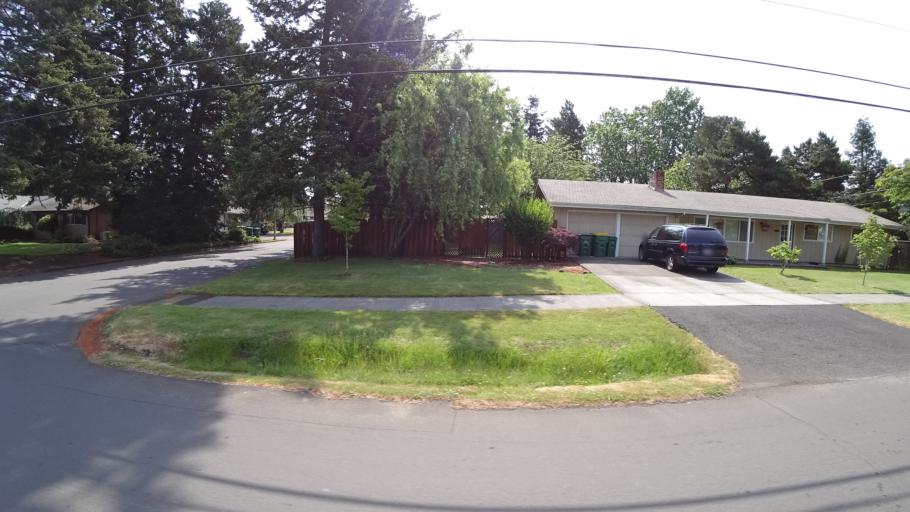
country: US
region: Oregon
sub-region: Washington County
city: Cedar Hills
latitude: 45.5037
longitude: -122.8198
